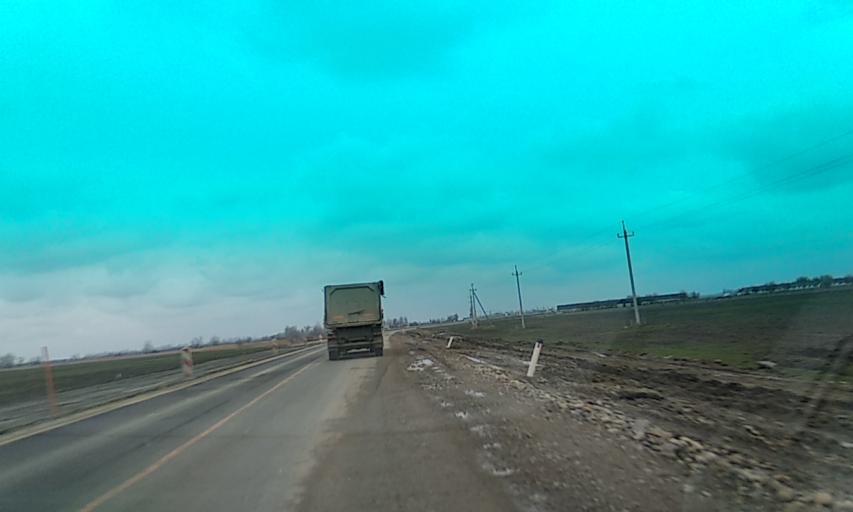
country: RU
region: Krasnodarskiy
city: Velikovechnoye
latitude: 44.9916
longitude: 39.7142
